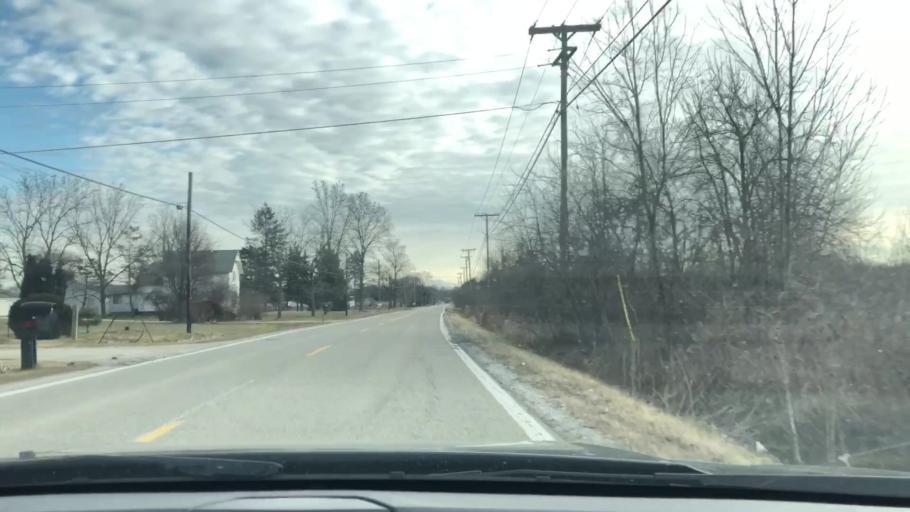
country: US
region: Michigan
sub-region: Macomb County
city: Shelby
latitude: 42.7303
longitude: -82.9874
